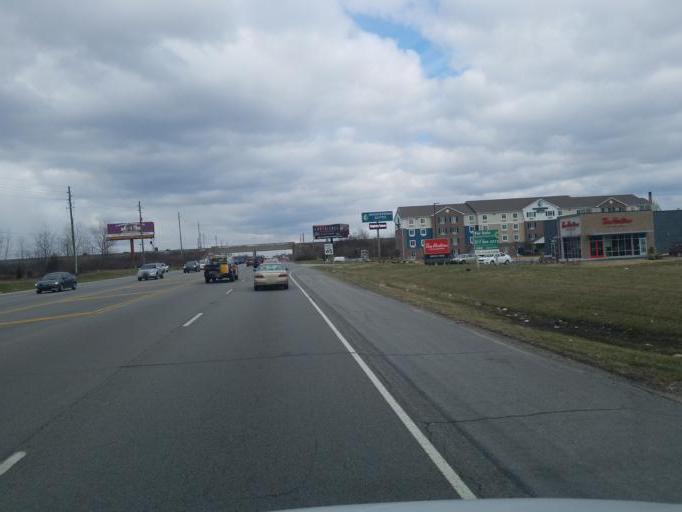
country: US
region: Indiana
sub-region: Marion County
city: Clermont
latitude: 39.7641
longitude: -86.3055
